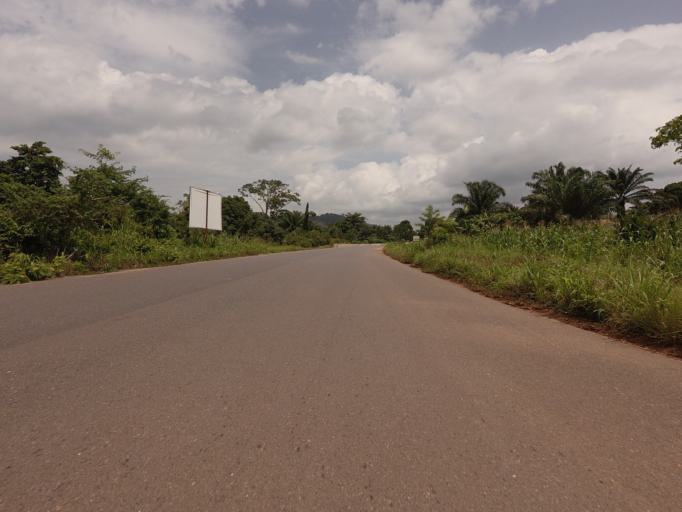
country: GH
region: Volta
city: Ho
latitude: 6.5150
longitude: 0.2186
